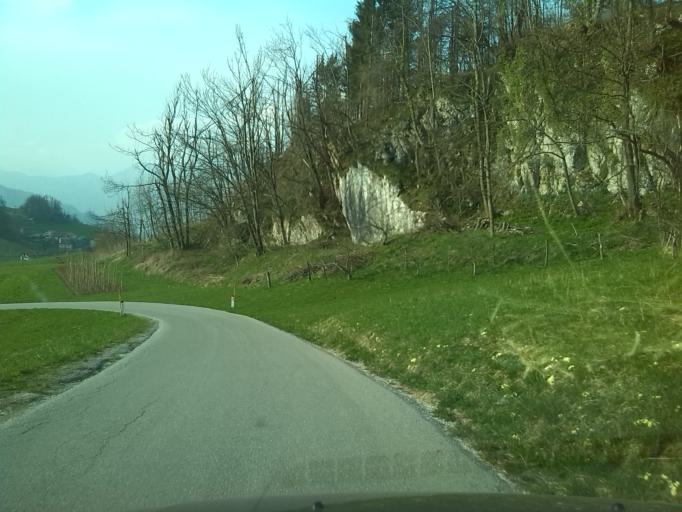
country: IT
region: Friuli Venezia Giulia
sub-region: Provincia di Udine
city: Cras
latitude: 46.2019
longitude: 13.6026
